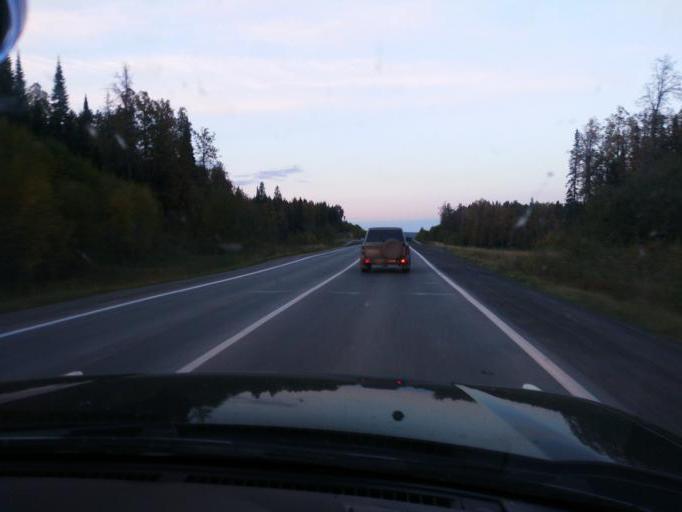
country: RU
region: Perm
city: Sylva
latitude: 58.2890
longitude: 56.7451
